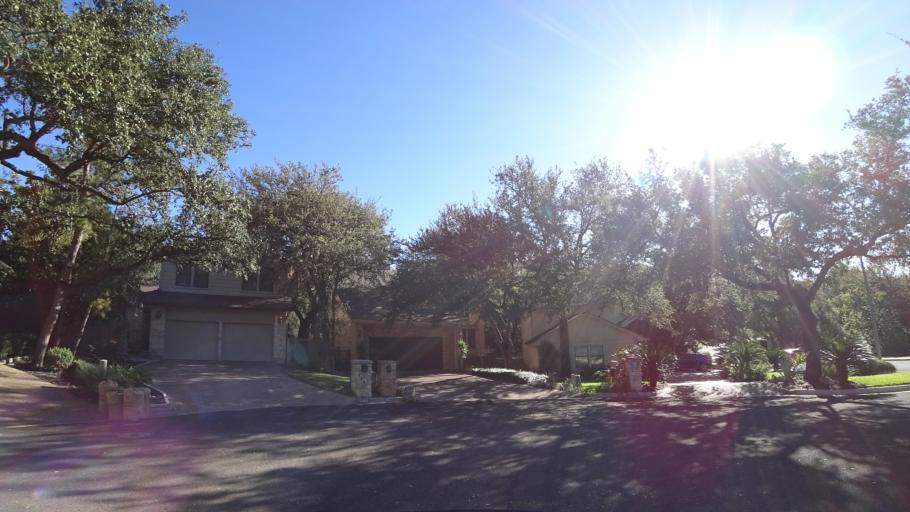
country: US
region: Texas
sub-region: Travis County
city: West Lake Hills
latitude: 30.3553
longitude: -97.7896
